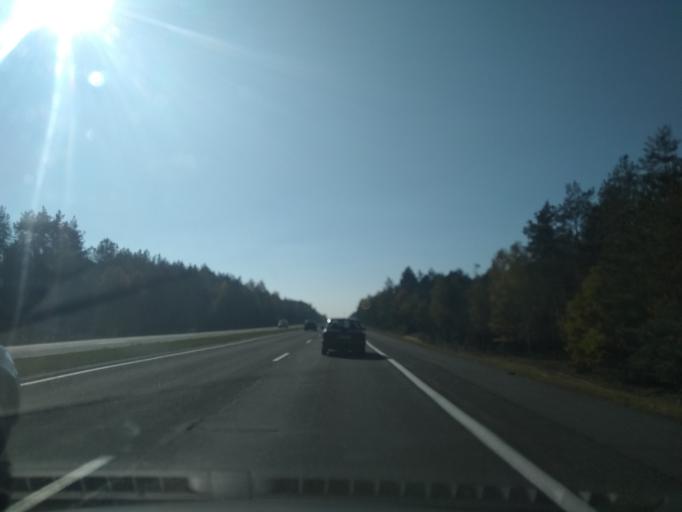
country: BY
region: Brest
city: Ivatsevichy
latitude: 52.8031
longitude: 25.5704
